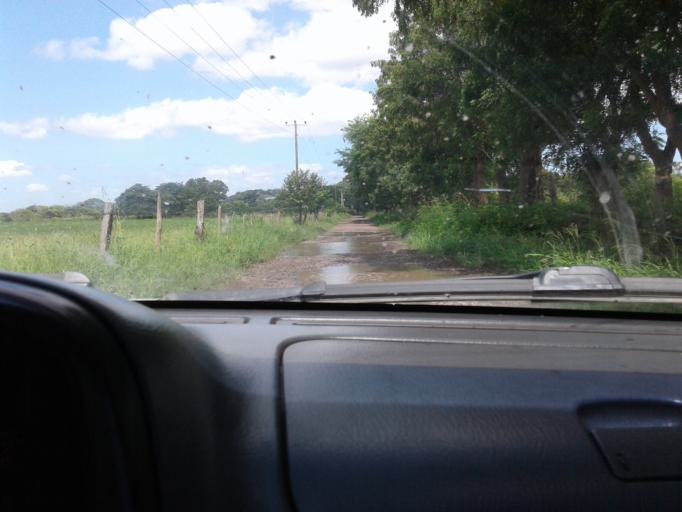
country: NI
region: Matagalpa
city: Ciudad Dario
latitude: 12.8424
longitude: -86.1470
